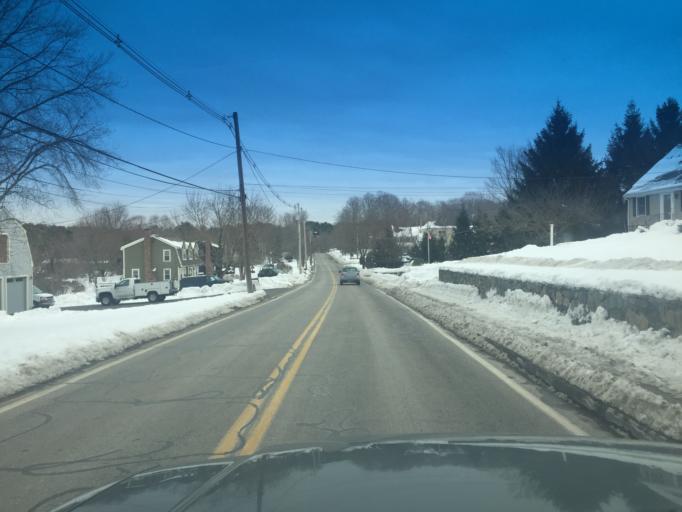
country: US
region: Massachusetts
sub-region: Norfolk County
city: Norfolk
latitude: 42.1031
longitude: -71.2812
